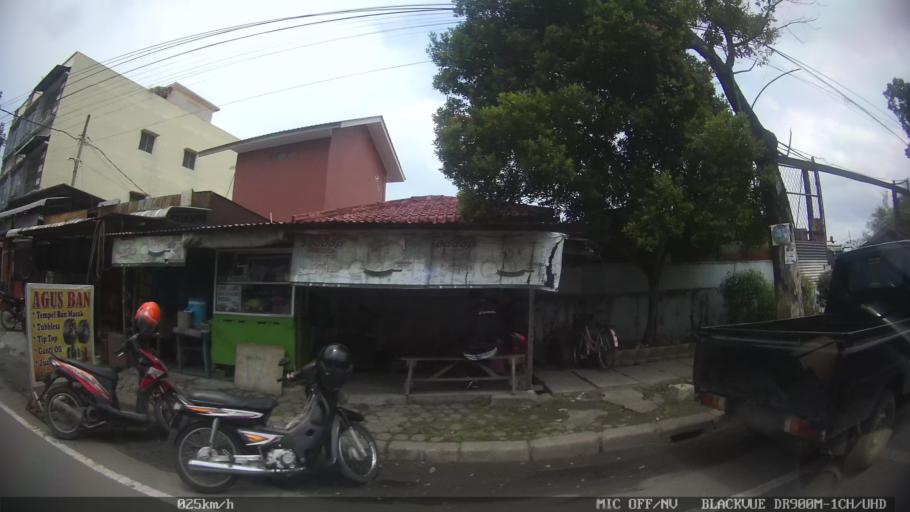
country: ID
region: North Sumatra
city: Medan
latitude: 3.6417
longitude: 98.6632
